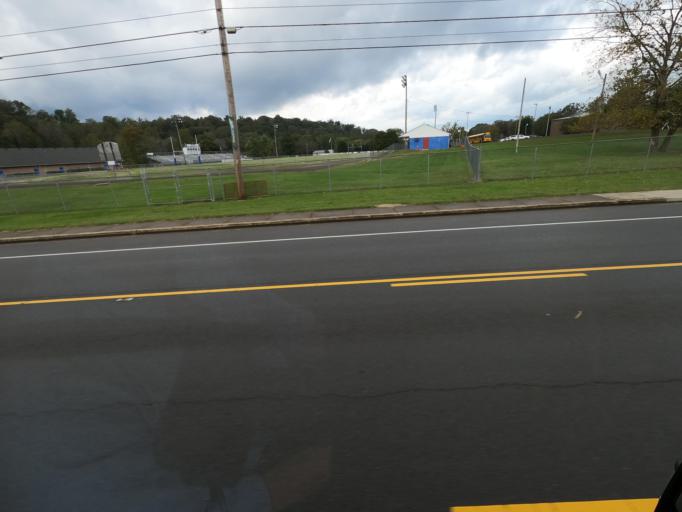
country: US
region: Tennessee
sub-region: Cheatham County
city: Kingston Springs
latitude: 36.0906
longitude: -87.0951
